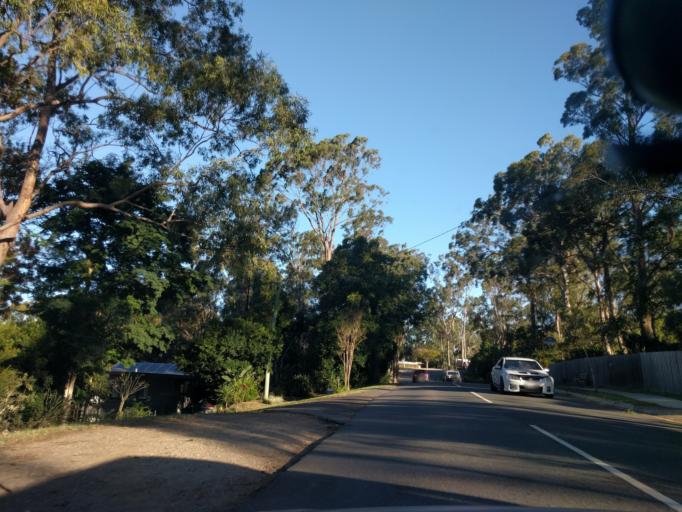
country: AU
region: Queensland
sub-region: Brisbane
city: Seventeen Mile Rocks
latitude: -27.5217
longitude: 152.9565
